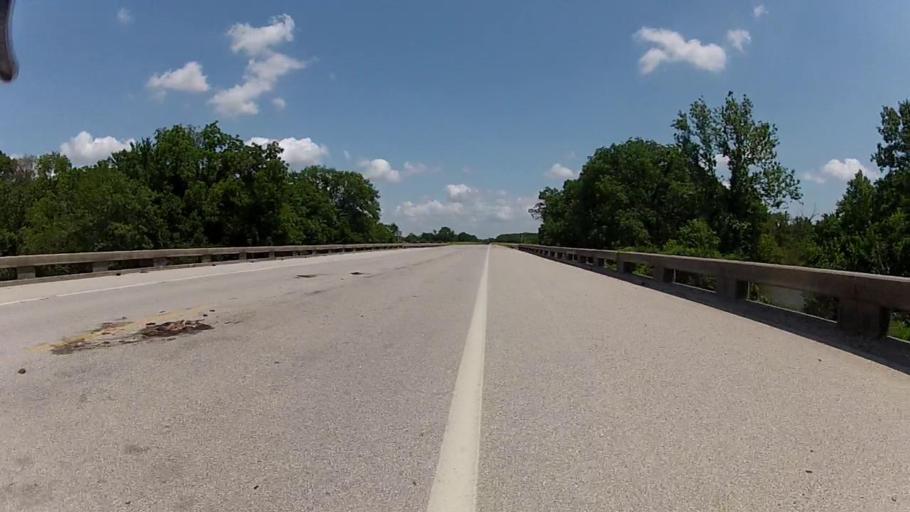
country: US
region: Kansas
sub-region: Labette County
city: Altamont
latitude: 37.1943
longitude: -95.3964
